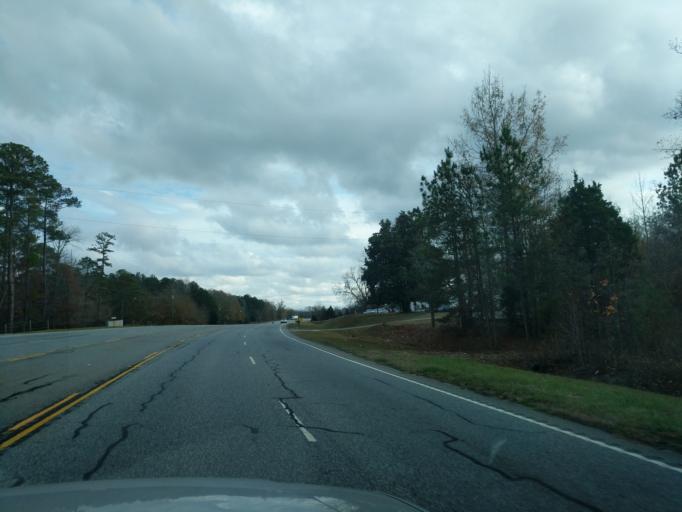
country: US
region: South Carolina
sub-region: Greenwood County
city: Ware Shoals
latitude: 34.4668
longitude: -82.2590
